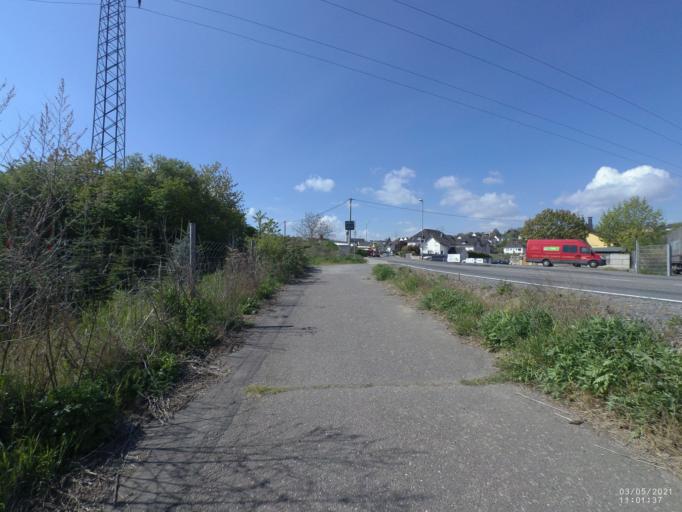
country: DE
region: Rheinland-Pfalz
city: Kettig
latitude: 50.4014
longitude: 7.4657
